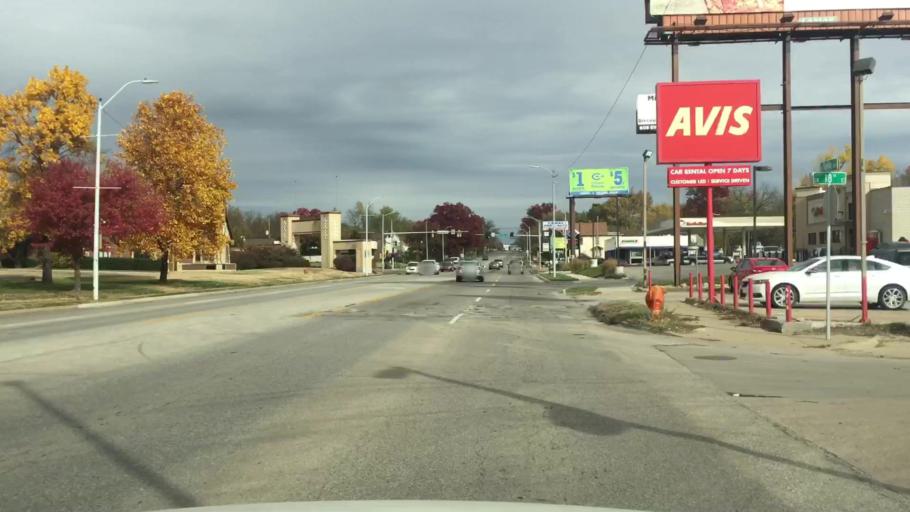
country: US
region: Kansas
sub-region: Shawnee County
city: Topeka
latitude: 39.0355
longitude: -95.6828
